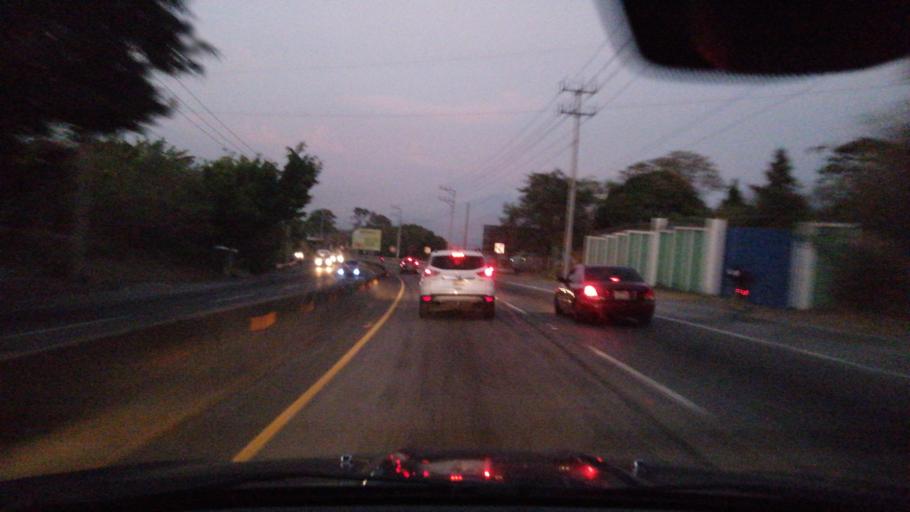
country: SV
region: San Salvador
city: Ayutuxtepeque
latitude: 13.7606
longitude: -89.2137
